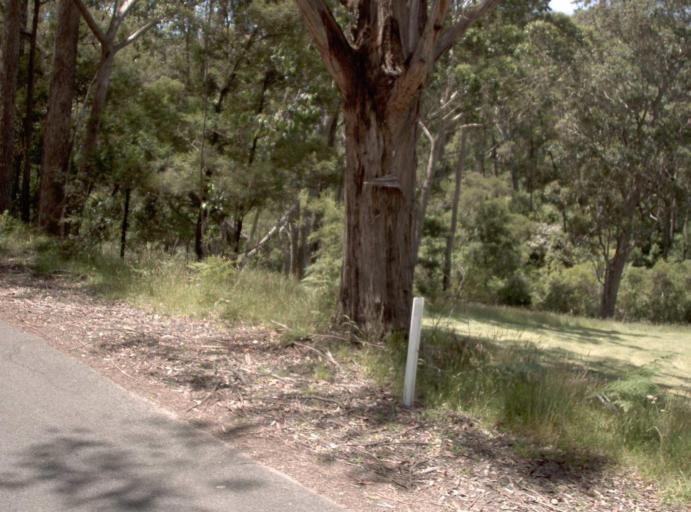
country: AU
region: New South Wales
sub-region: Bombala
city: Bombala
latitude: -37.5267
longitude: 148.9316
